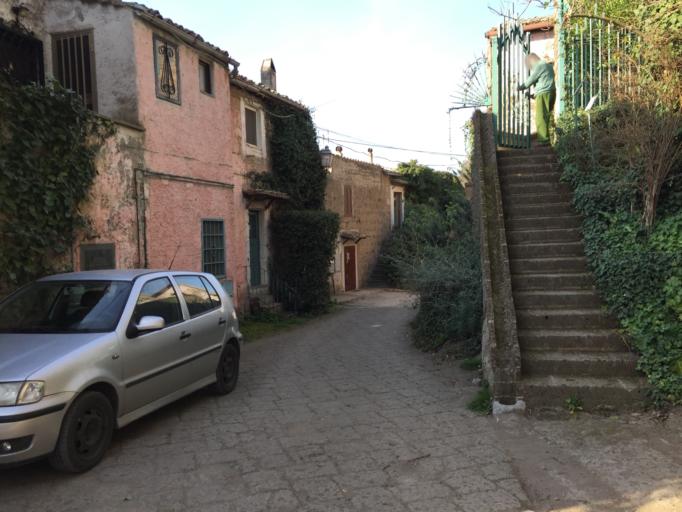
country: IT
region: Latium
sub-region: Provincia di Viterbo
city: Calcata Nuova
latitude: 42.2169
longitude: 12.4214
